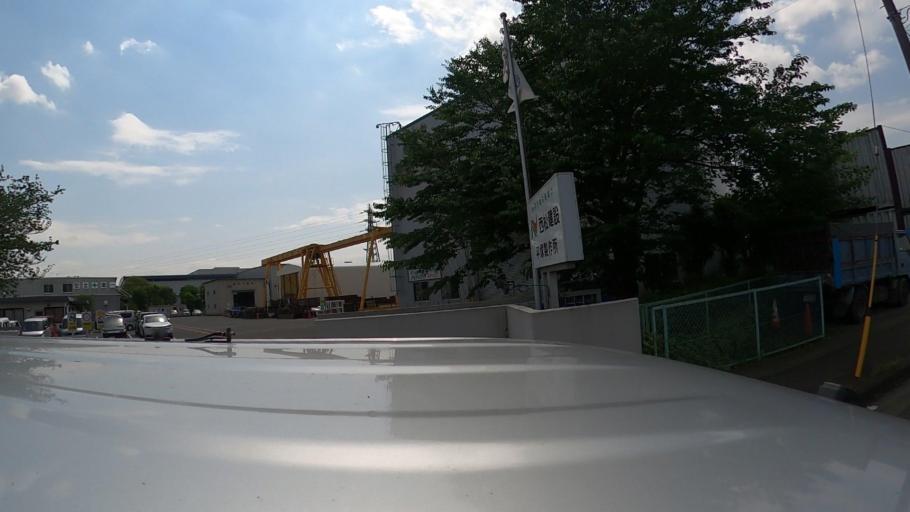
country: JP
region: Kanagawa
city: Chigasaki
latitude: 35.3626
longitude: 139.3737
